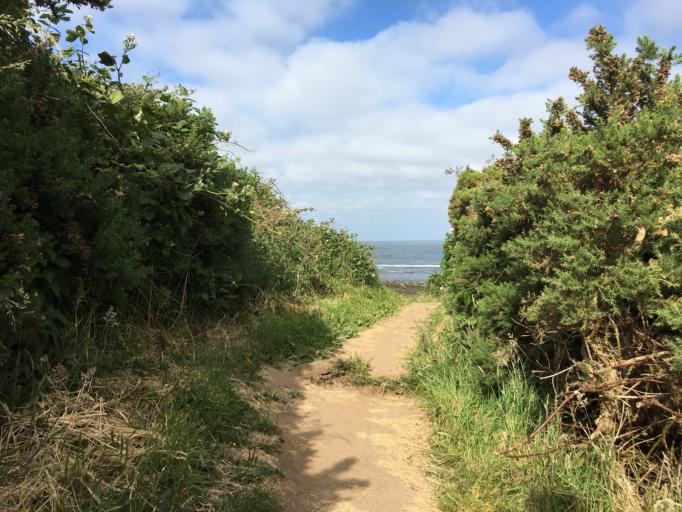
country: GB
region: England
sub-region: Northumberland
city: Alnmouth
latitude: 55.4426
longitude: -1.5918
